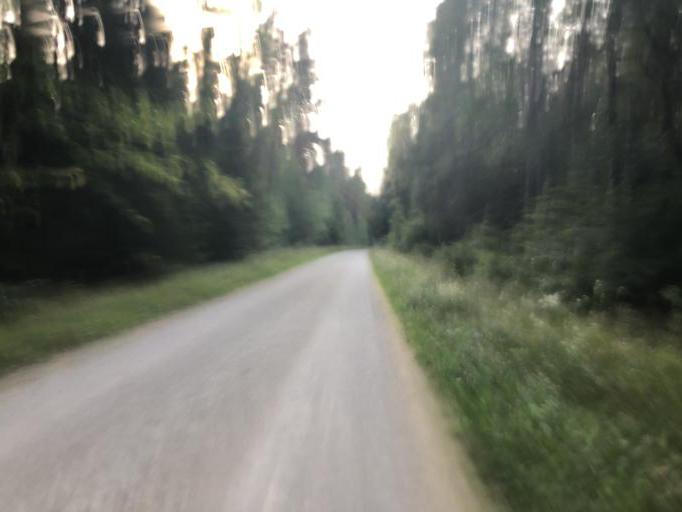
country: DE
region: Bavaria
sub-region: Regierungsbezirk Mittelfranken
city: Buckenhof
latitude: 49.5770
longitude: 11.0458
